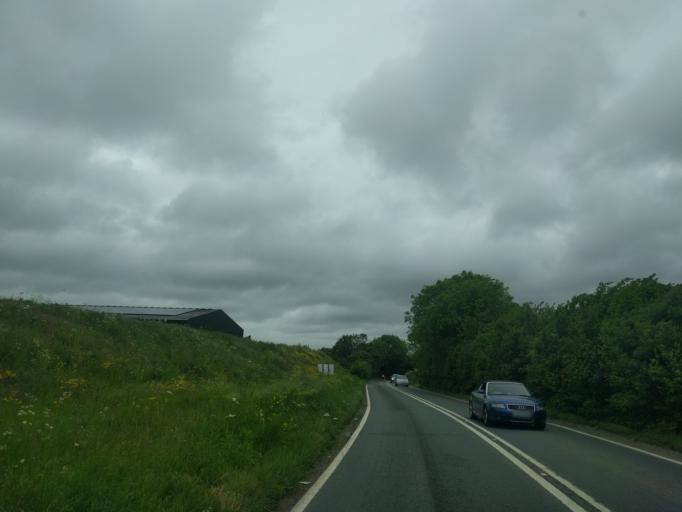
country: GB
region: England
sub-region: Wiltshire
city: Wingfield
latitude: 51.2766
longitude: -2.2795
